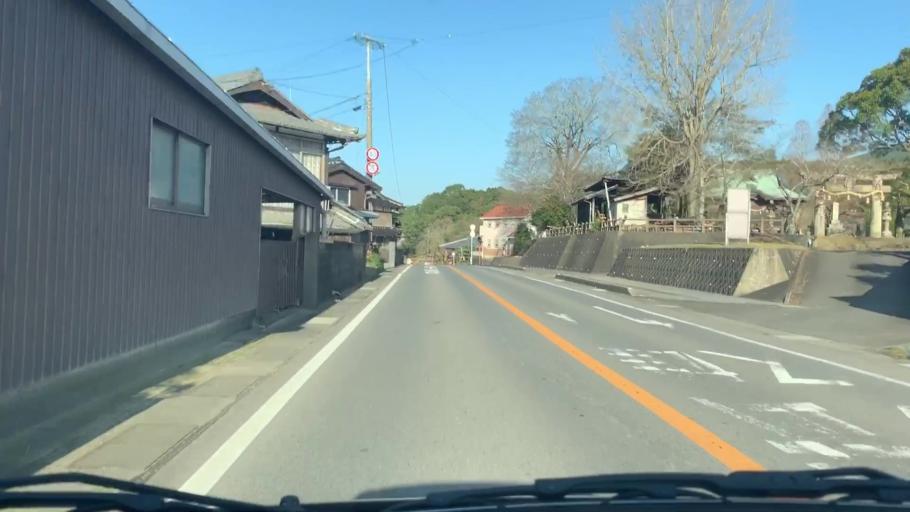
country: JP
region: Saga Prefecture
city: Takeocho-takeo
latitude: 33.2523
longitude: 129.9946
